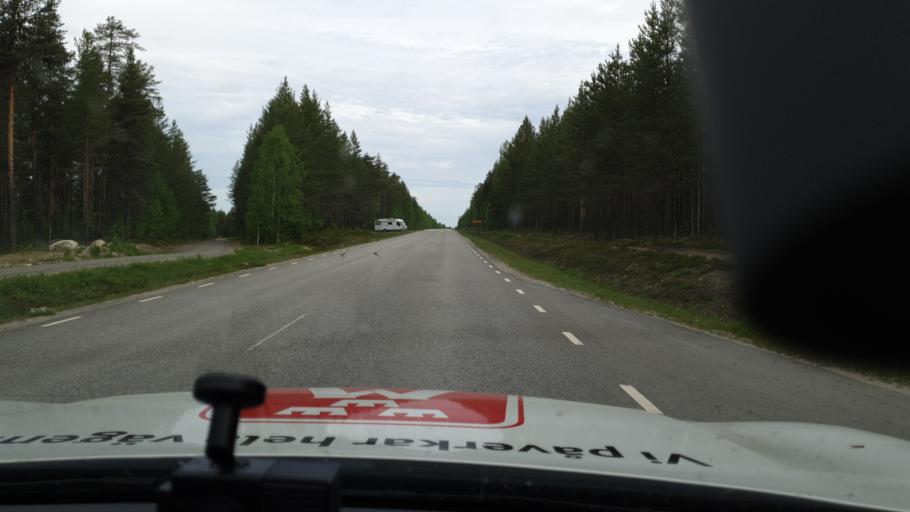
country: SE
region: Vaesterbotten
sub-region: Lycksele Kommun
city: Lycksele
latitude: 64.6125
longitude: 18.6952
